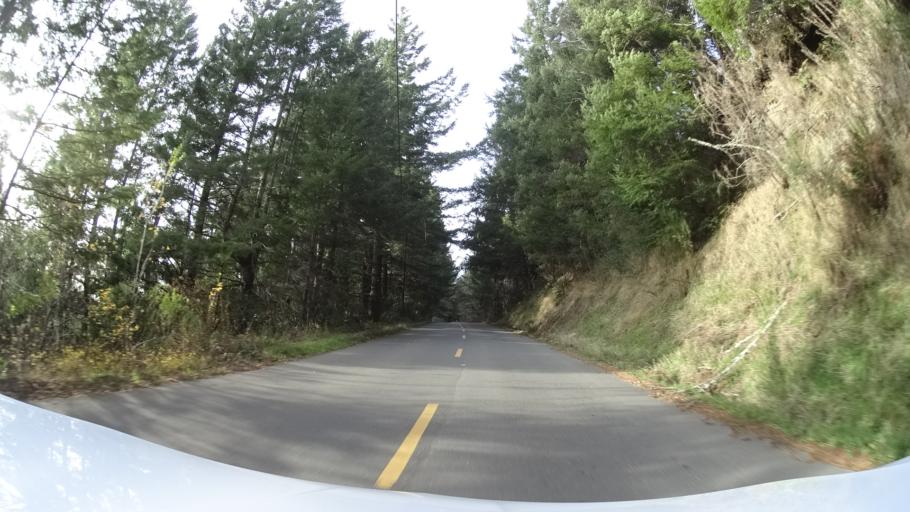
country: US
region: California
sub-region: Humboldt County
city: Ferndale
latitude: 40.5345
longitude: -124.2705
